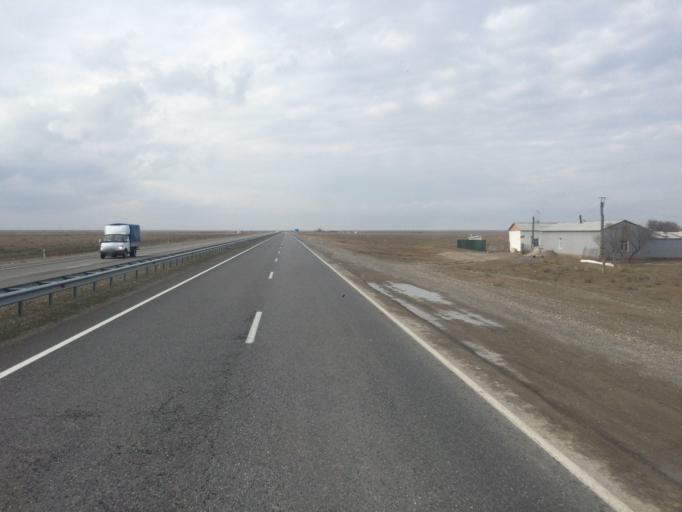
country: KZ
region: Ongtustik Qazaqstan
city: Turkestan
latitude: 43.5272
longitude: 67.7909
